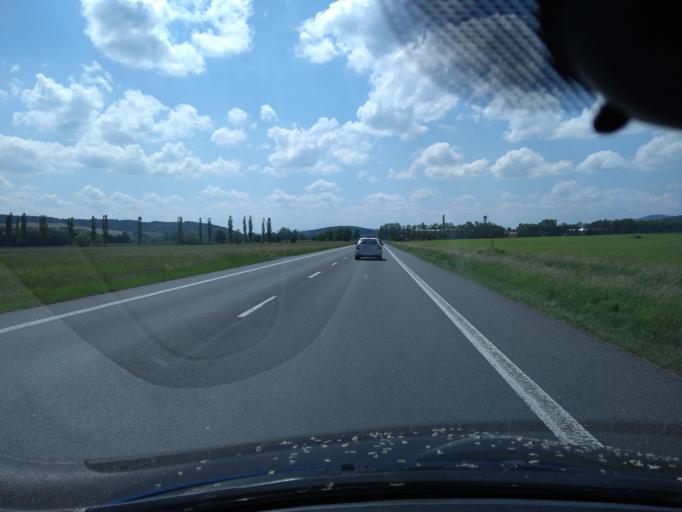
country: CZ
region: Plzensky
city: Svihov
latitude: 49.4916
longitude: 13.2881
